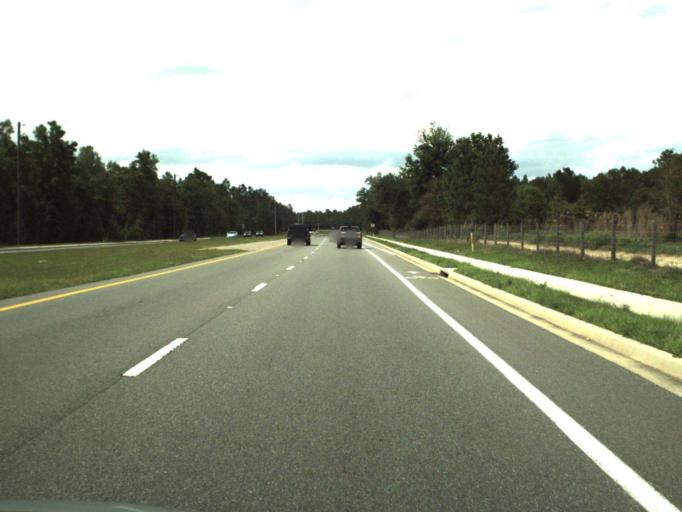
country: US
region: Florida
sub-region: Marion County
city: Ocala
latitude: 29.1970
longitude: -82.0536
